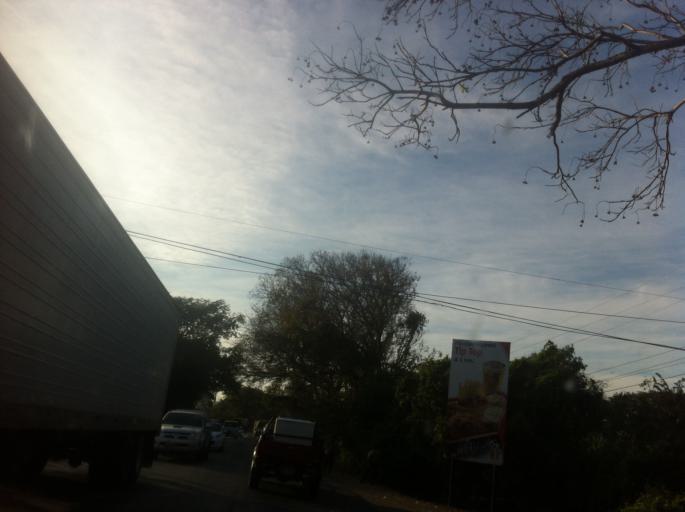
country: NI
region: Rivas
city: Rivas
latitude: 11.4169
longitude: -85.7981
